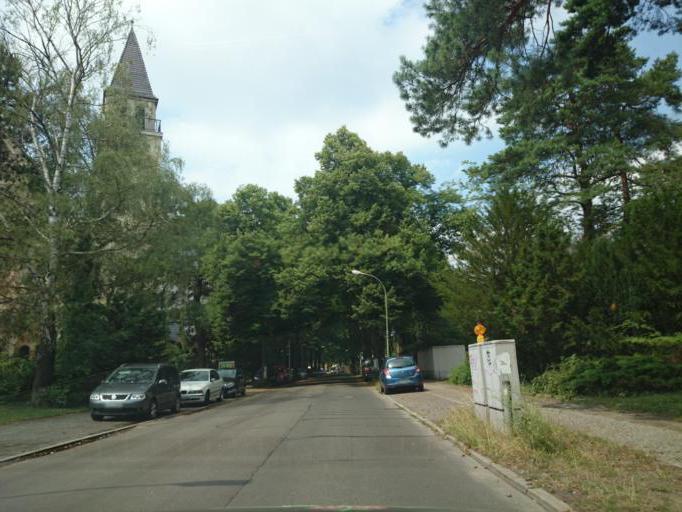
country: DE
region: Berlin
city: Nikolassee
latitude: 52.4377
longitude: 13.2203
